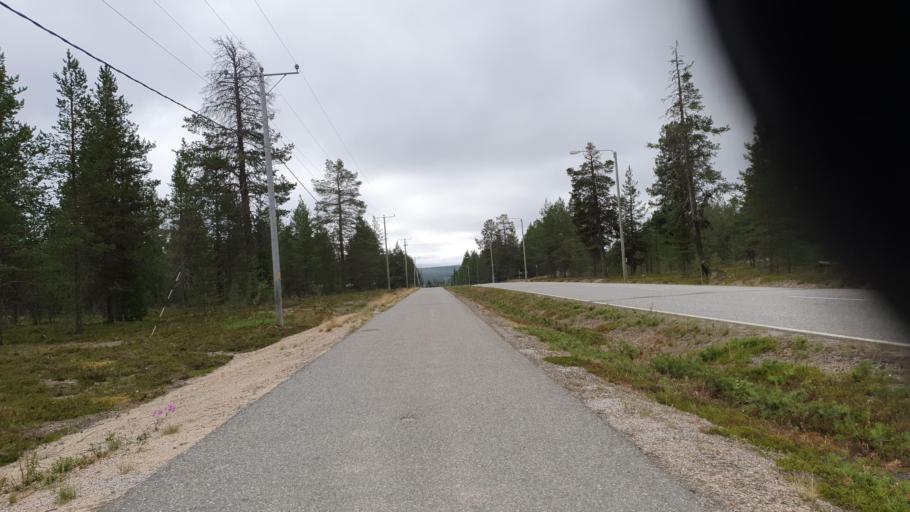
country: FI
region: Lapland
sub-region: Tunturi-Lappi
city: Kolari
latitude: 67.6245
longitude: 24.1551
